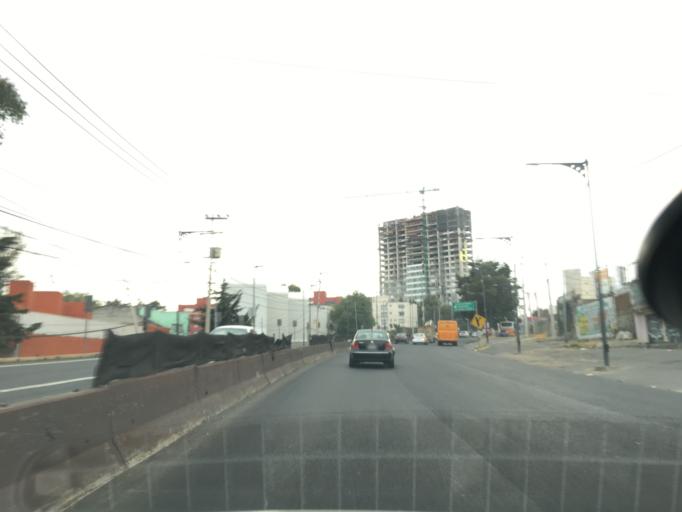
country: MX
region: Mexico City
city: Cuajimalpa
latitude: 19.3519
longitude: -99.2956
